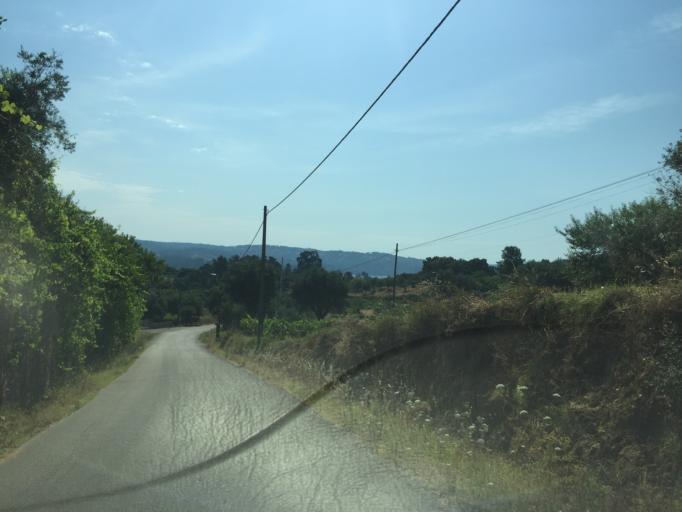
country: PT
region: Santarem
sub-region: Ferreira do Zezere
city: Ferreira do Zezere
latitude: 39.6069
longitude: -8.2869
